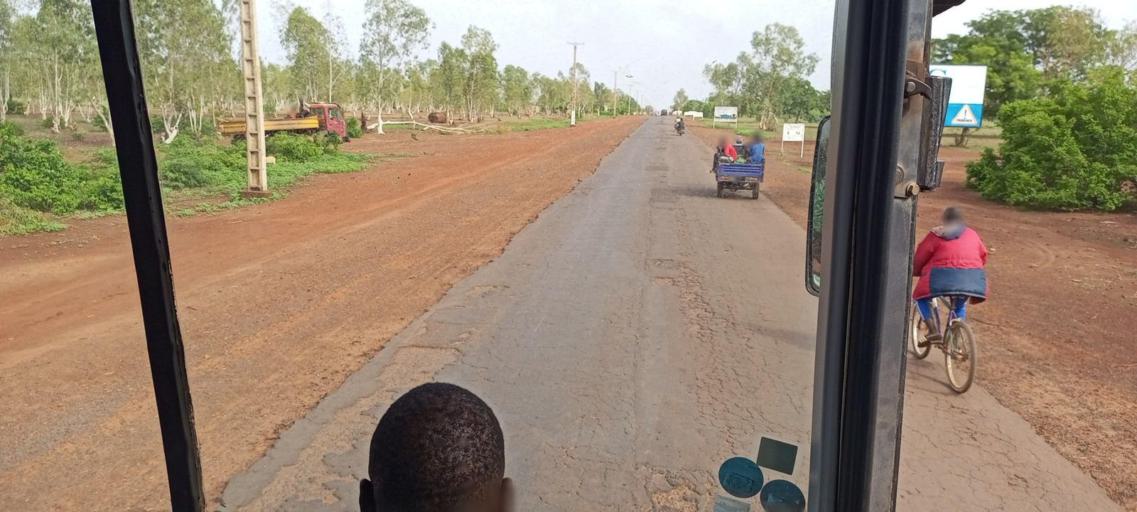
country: ML
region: Sikasso
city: Koutiala
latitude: 12.4354
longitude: -5.4796
